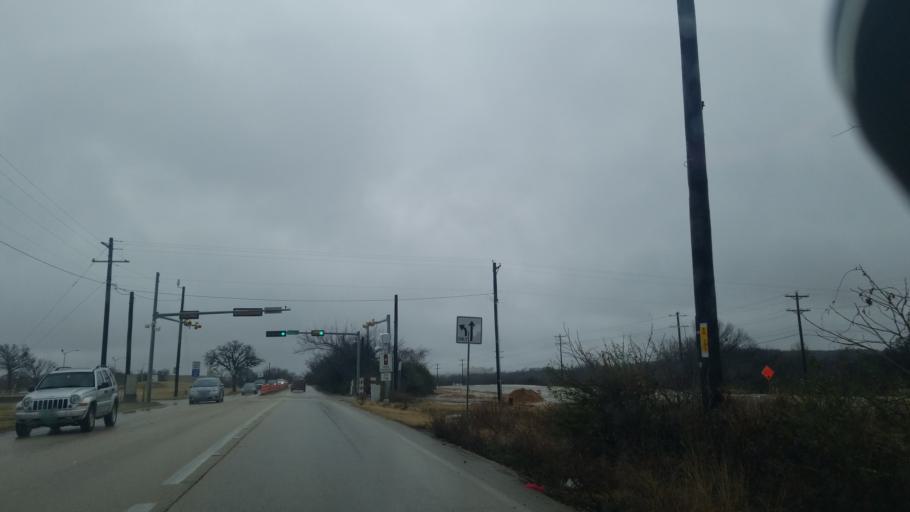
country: US
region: Texas
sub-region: Denton County
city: Corinth
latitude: 33.1957
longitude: -97.0848
